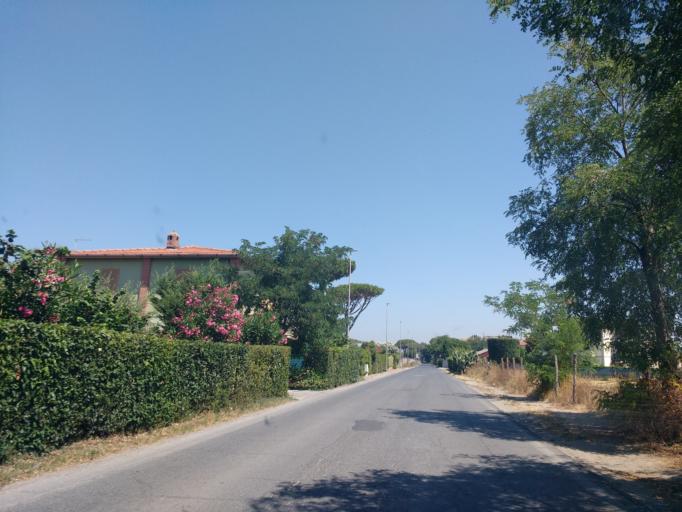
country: IT
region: Latium
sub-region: Citta metropolitana di Roma Capitale
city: Fregene
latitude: 41.8511
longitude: 12.2181
